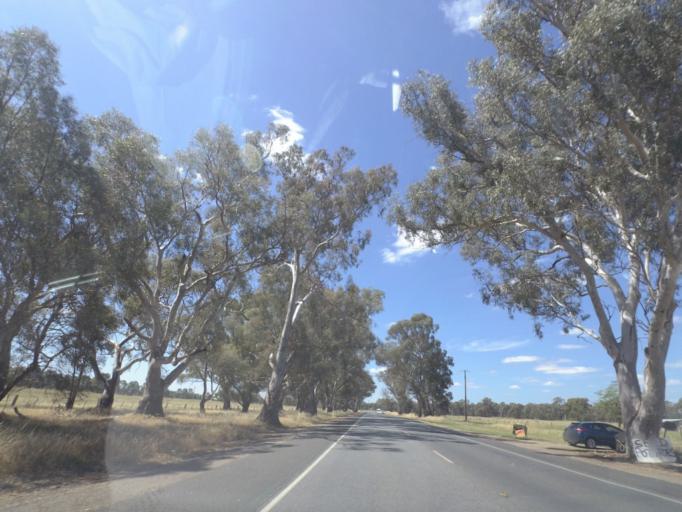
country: AU
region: Victoria
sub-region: Wangaratta
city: Wangaratta
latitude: -36.4017
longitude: 146.2762
